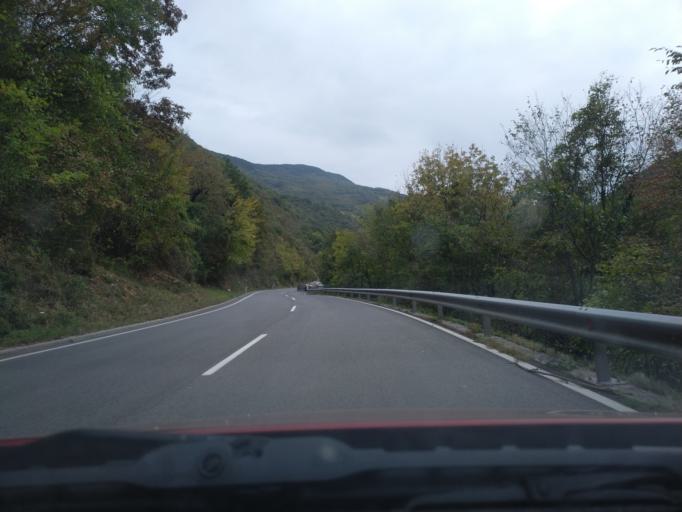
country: SI
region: Nova Gorica
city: Solkan
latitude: 45.9896
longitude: 13.6476
